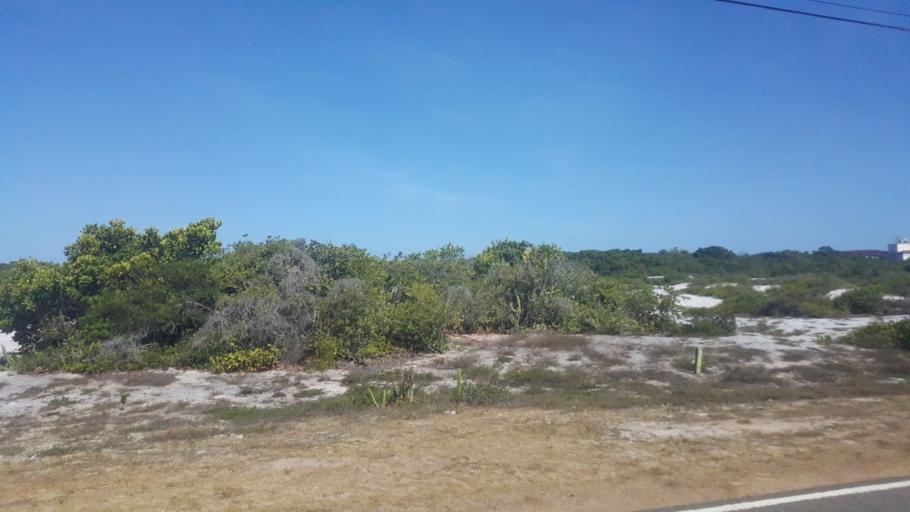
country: BR
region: Bahia
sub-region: Mata De Sao Joao
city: Mata de Sao Joao
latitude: -12.4344
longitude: -37.9201
